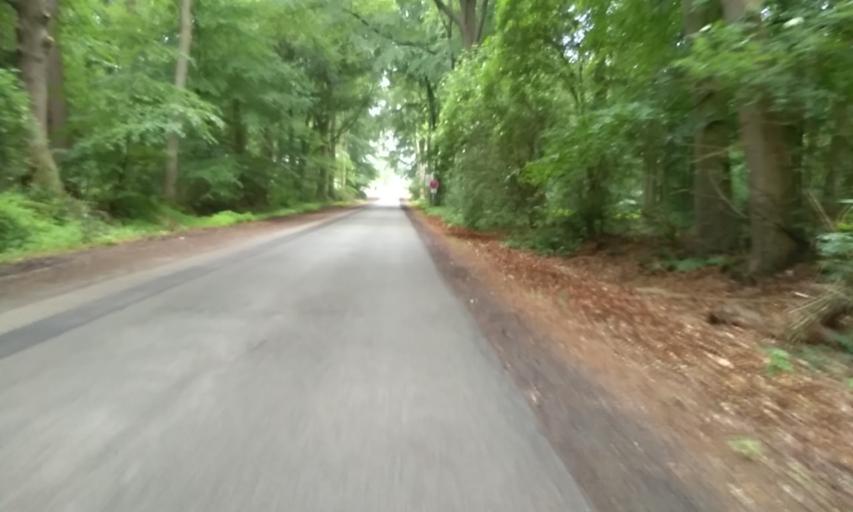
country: DE
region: Lower Saxony
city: Nottensdorf
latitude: 53.4714
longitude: 9.6351
